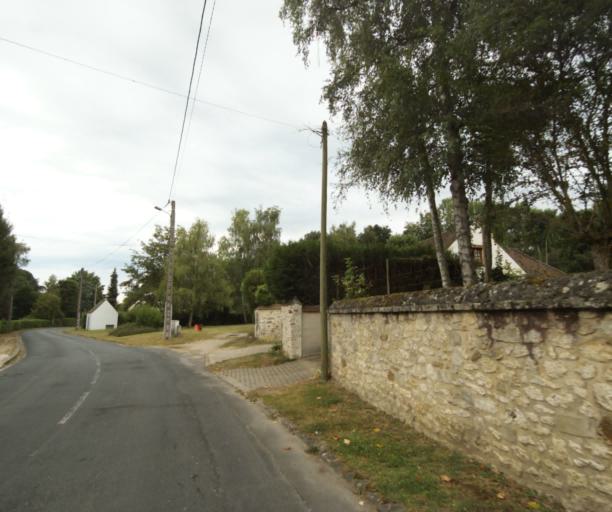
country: FR
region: Ile-de-France
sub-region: Departement de Seine-et-Marne
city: Cely
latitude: 48.4627
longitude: 2.5218
